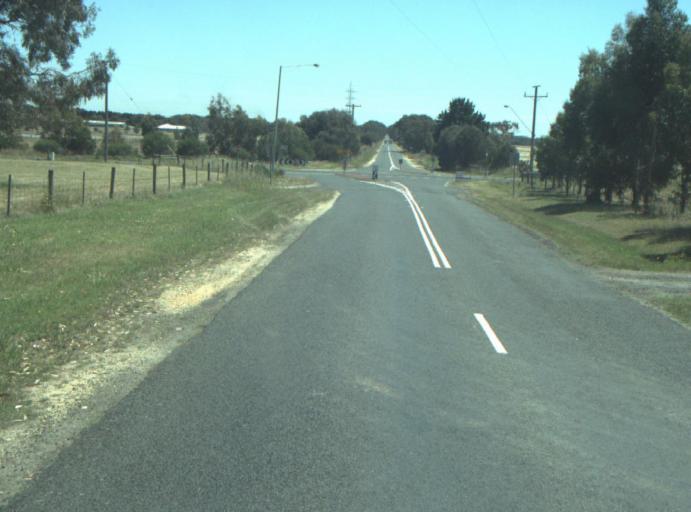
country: AU
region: Victoria
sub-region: Greater Geelong
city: Breakwater
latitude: -38.2515
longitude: 144.3506
